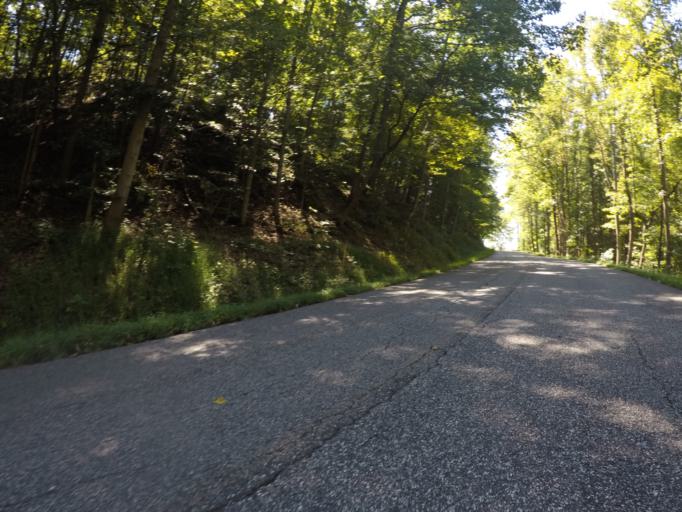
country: US
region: Kentucky
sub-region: Boyd County
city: Meads
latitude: 38.4199
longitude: -82.6628
